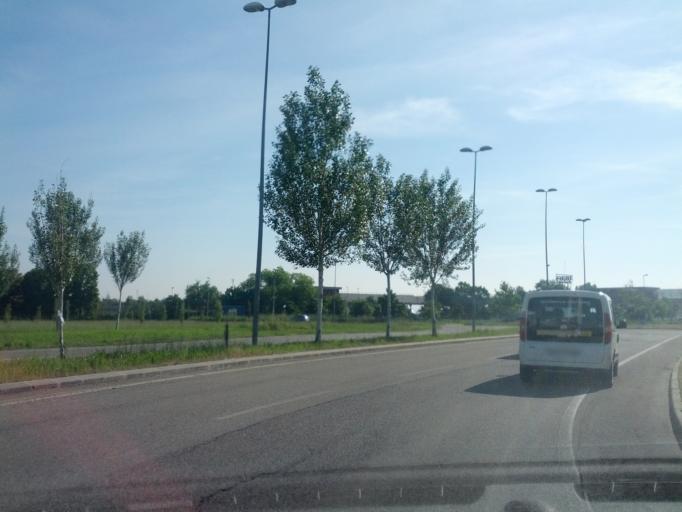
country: IT
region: Emilia-Romagna
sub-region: Provincia di Reggio Emilia
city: Reggio nell'Emilia
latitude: 44.7307
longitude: 10.6400
